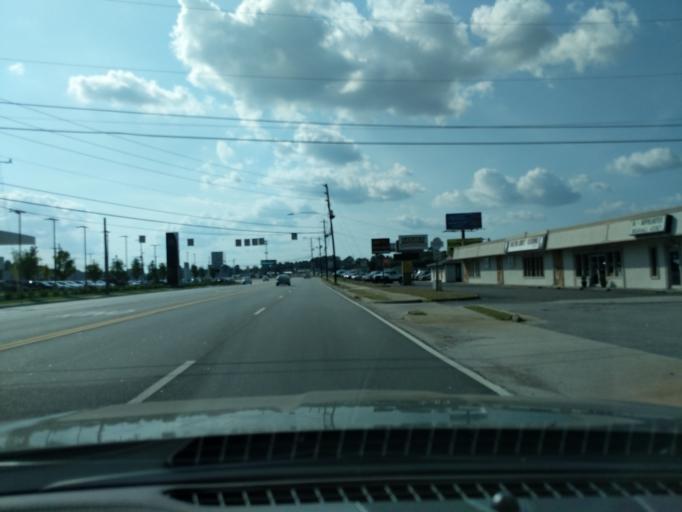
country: US
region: Georgia
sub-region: Columbia County
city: Martinez
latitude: 33.5162
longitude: -82.0706
